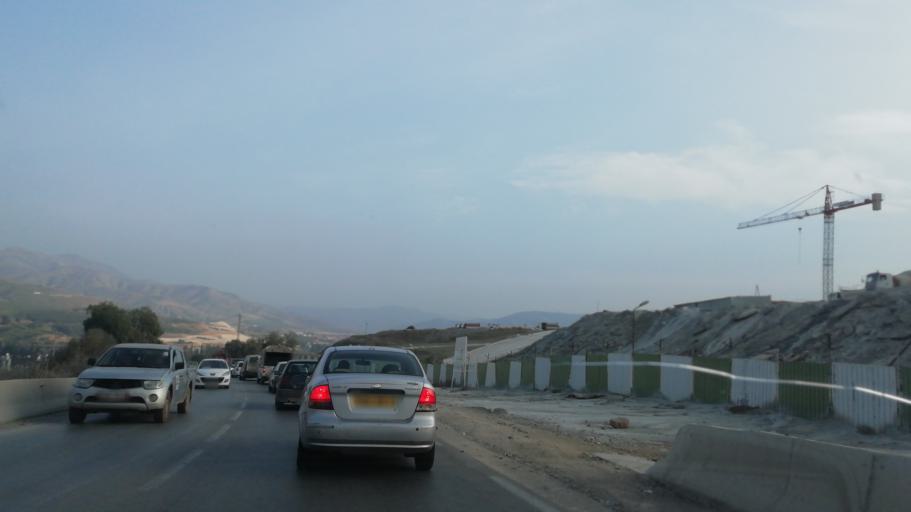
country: DZ
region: Mascara
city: Bou Hanifia el Hamamat
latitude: 35.4716
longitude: -0.0151
